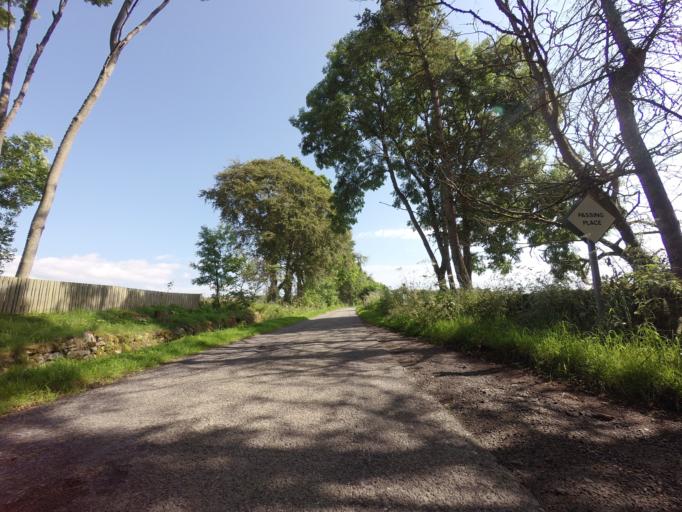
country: GB
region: Scotland
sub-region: Highland
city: Alness
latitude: 57.7129
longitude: -4.2220
